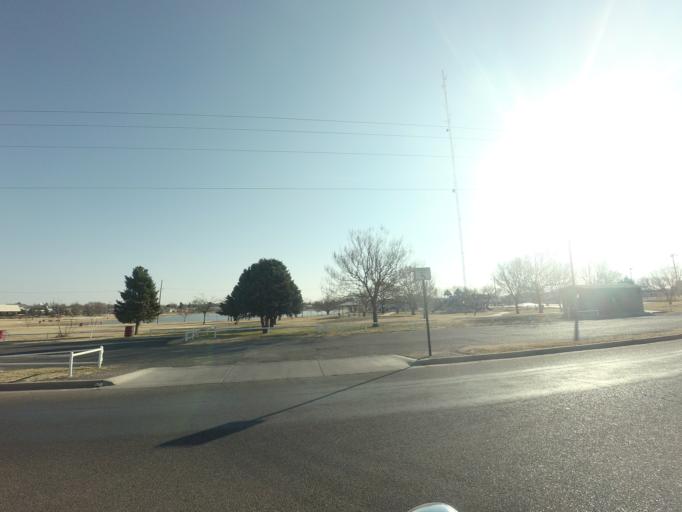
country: US
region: New Mexico
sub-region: Curry County
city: Clovis
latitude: 34.4175
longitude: -103.2098
